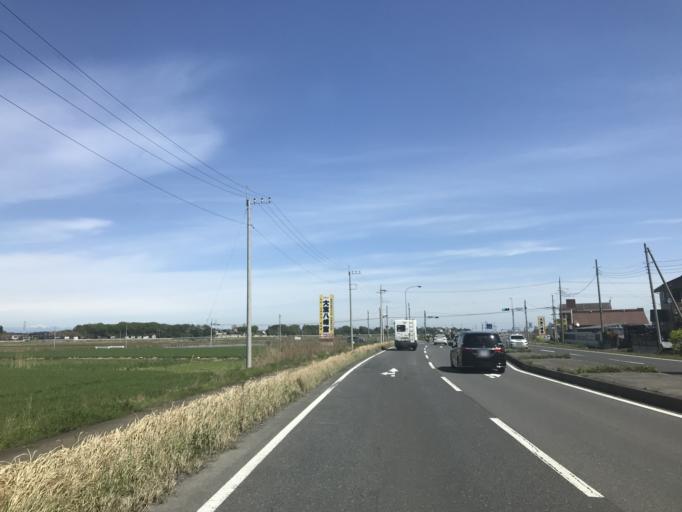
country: JP
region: Ibaraki
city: Ishige
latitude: 36.2011
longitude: 139.9841
